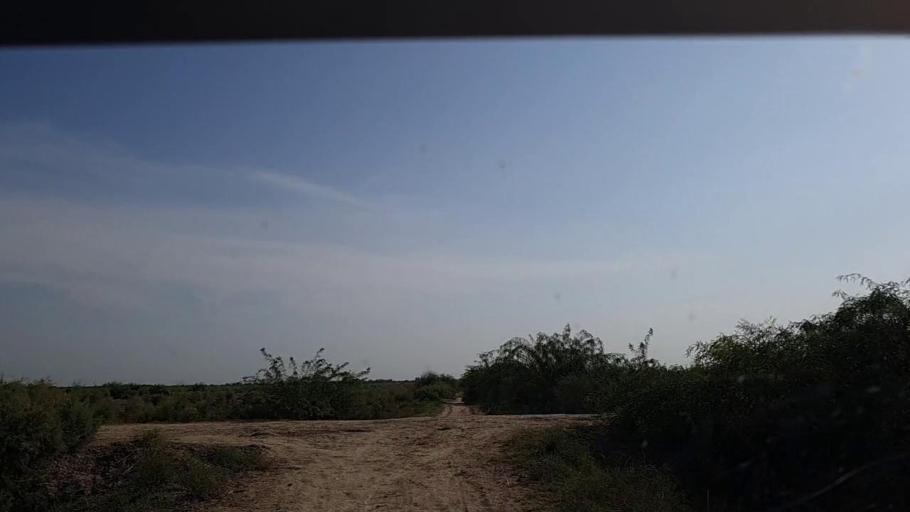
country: PK
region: Sindh
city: Adilpur
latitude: 27.9014
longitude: 69.2311
